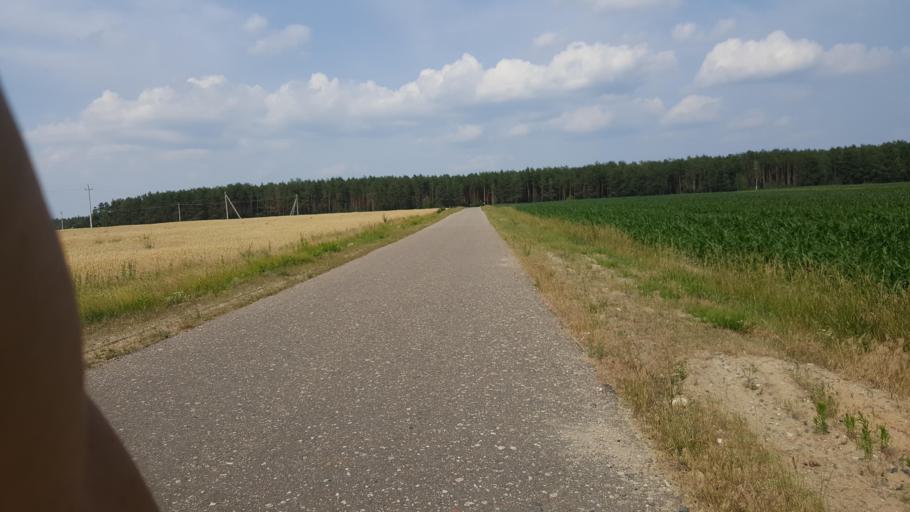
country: BY
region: Brest
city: Kamyanyets
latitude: 52.3616
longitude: 23.8063
